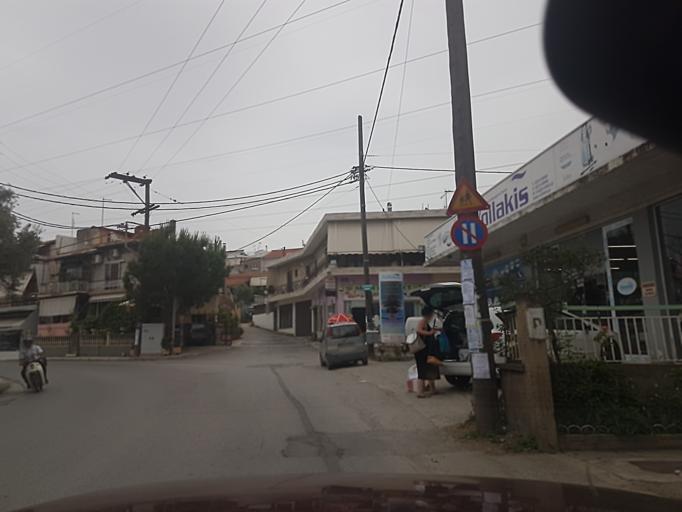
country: GR
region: Central Greece
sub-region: Nomos Evvoias
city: Chalkida
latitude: 38.4651
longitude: 23.6184
